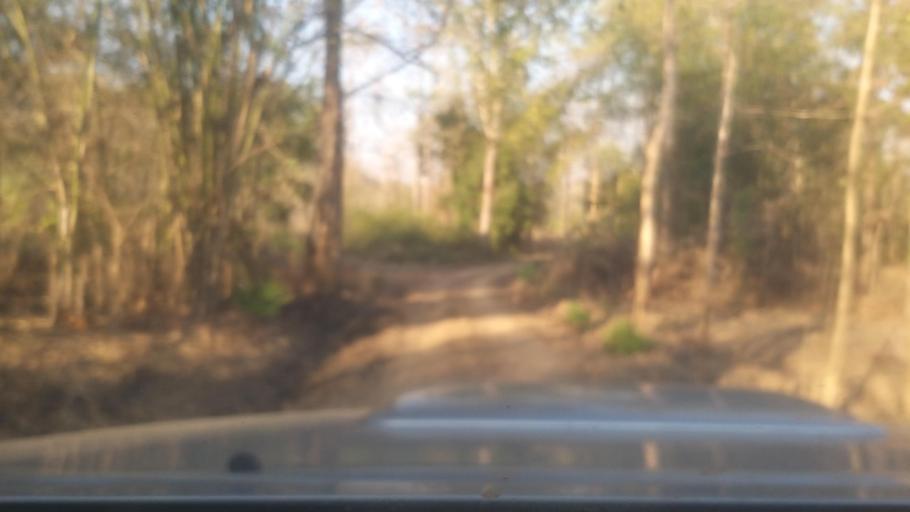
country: TH
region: Phrae
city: Nong Muang Khai
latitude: 18.2841
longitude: 100.0219
